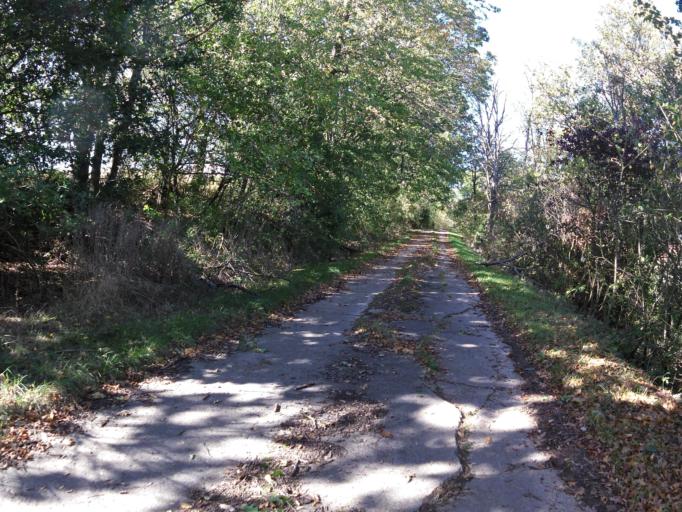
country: DE
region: Bavaria
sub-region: Regierungsbezirk Unterfranken
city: Hettstadt
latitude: 49.8287
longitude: 9.8296
